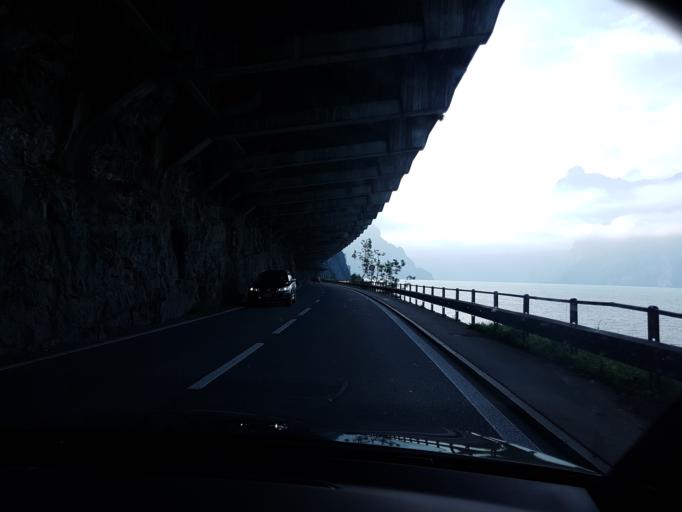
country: CH
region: Schwyz
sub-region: Bezirk Schwyz
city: Ingenbohl
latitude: 46.9661
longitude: 8.6139
